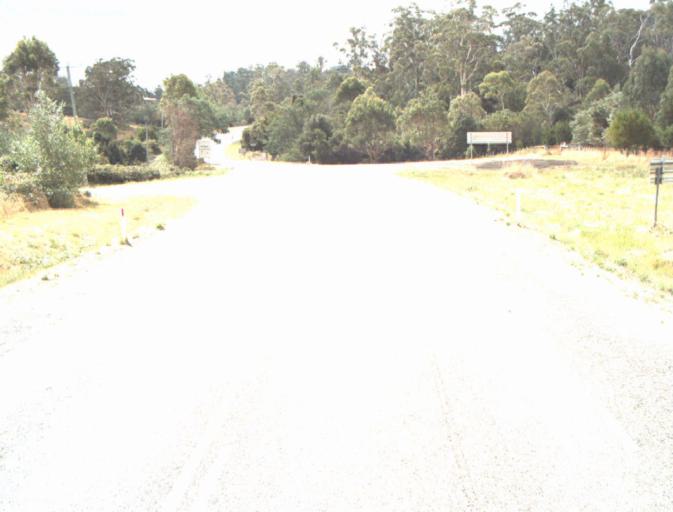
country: AU
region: Tasmania
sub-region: Launceston
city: Mayfield
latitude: -41.3090
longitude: 147.0506
